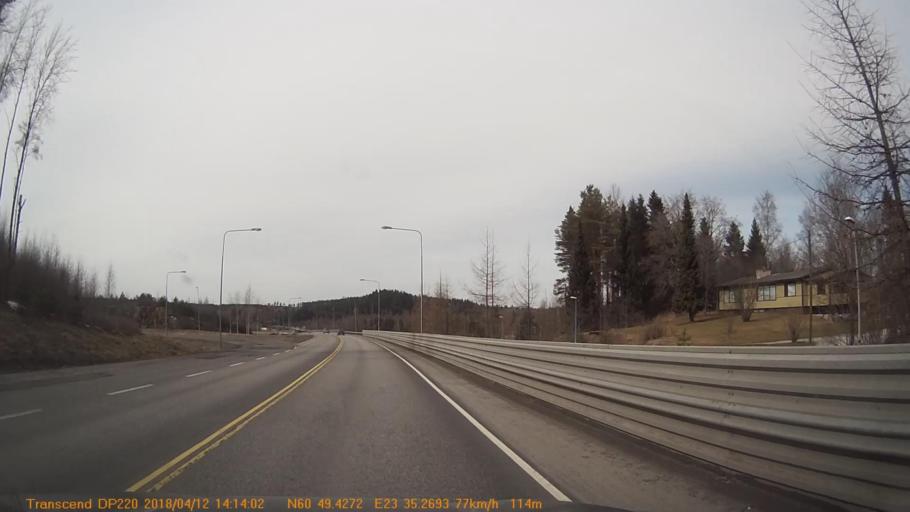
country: FI
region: Haeme
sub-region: Forssa
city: Forssa
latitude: 60.8241
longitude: 23.5874
